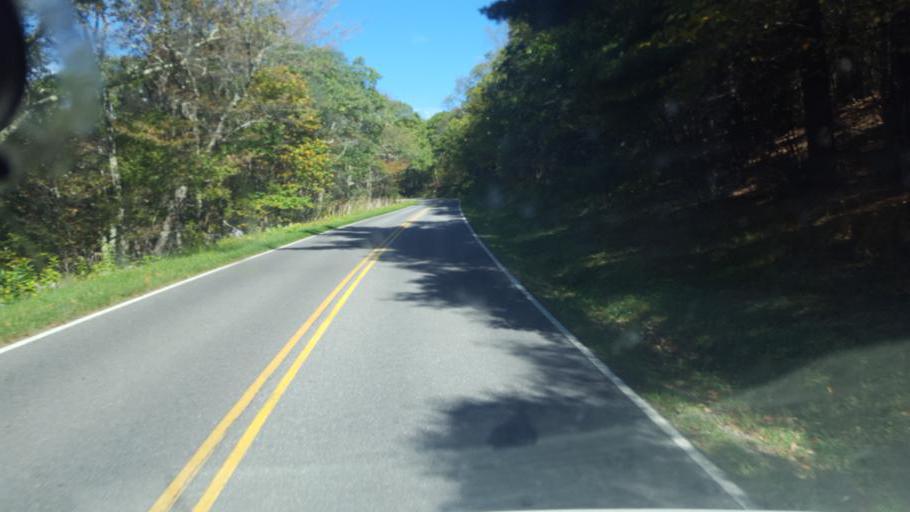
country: US
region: Virginia
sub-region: Page County
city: Stanley
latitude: 38.4354
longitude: -78.4801
